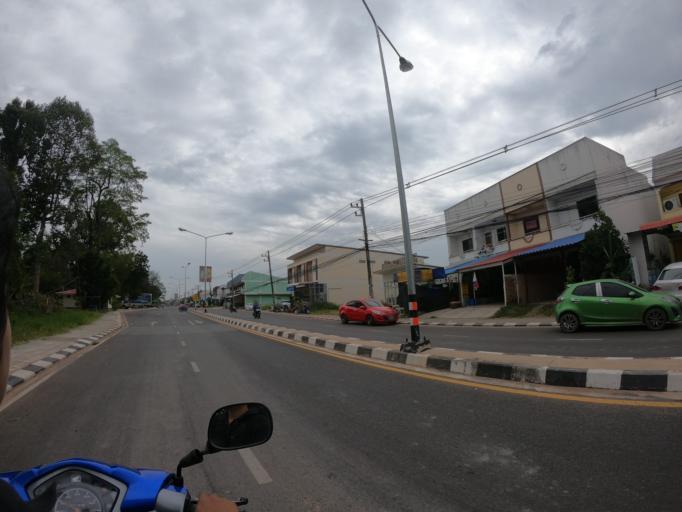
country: TH
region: Roi Et
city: Chiang Khwan
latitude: 16.1498
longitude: 103.8665
